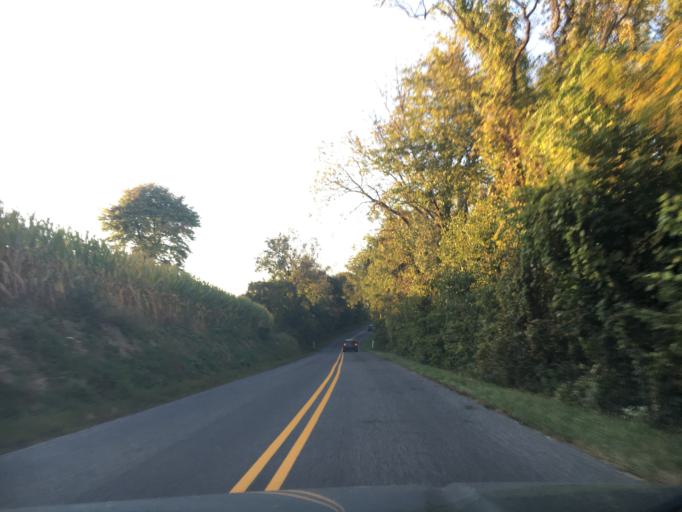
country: US
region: Pennsylvania
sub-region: Lehigh County
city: Schnecksville
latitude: 40.6101
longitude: -75.6445
